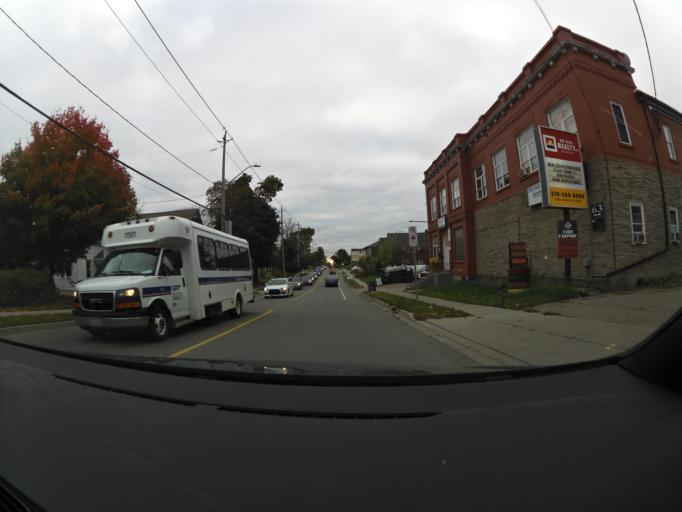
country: CA
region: Ontario
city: Kitchener
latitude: 43.4448
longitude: -80.4906
